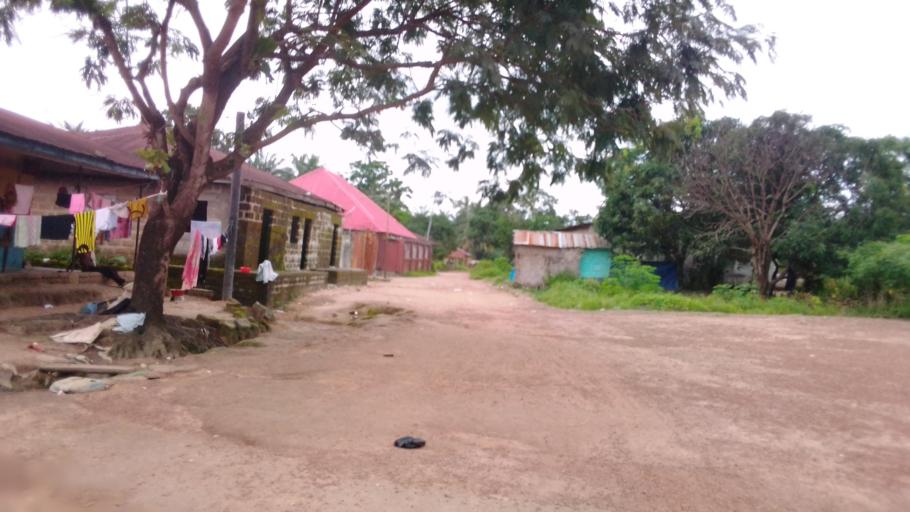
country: SL
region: Northern Province
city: Makeni
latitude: 8.8795
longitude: -12.0421
